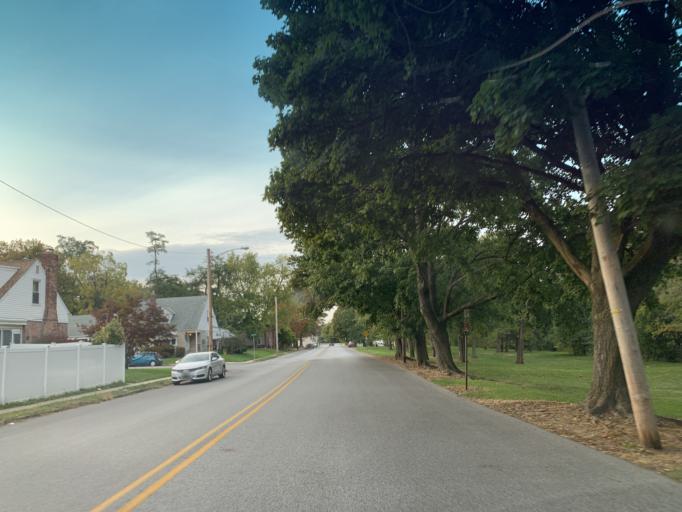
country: US
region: Pennsylvania
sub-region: York County
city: Valley View
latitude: 39.9546
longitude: -76.7140
